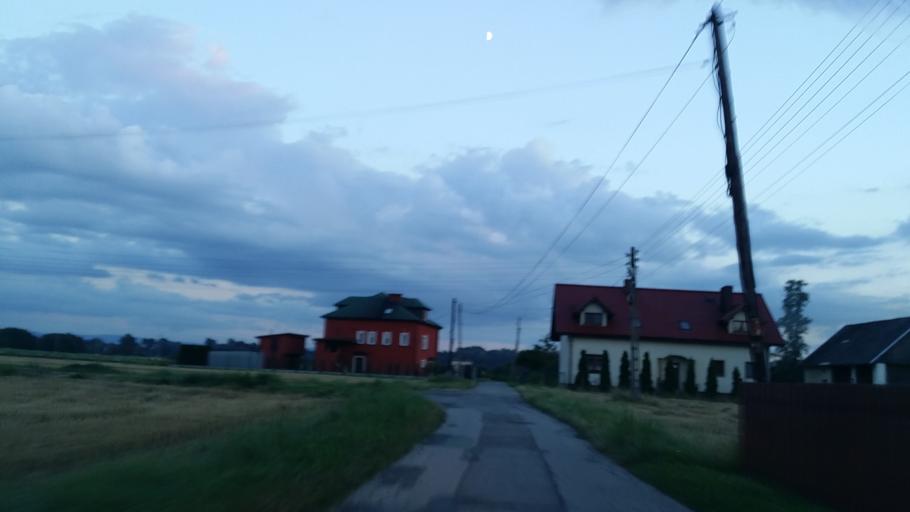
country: PL
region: Lesser Poland Voivodeship
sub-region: Powiat oswiecimski
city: Przeciszow
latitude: 50.0177
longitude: 19.3776
